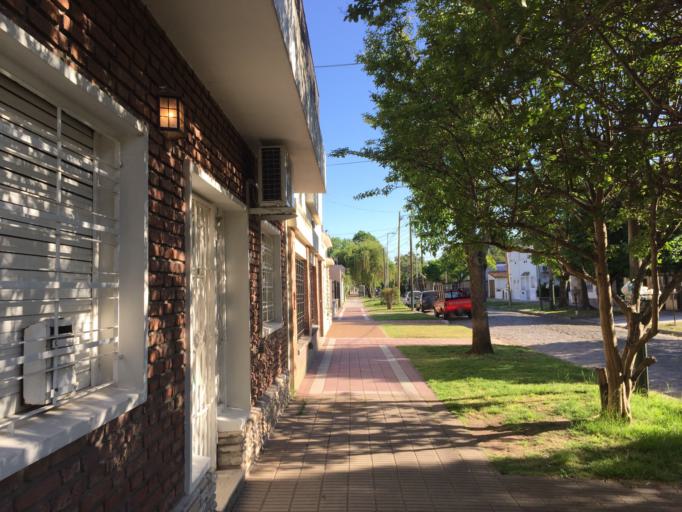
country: AR
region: Buenos Aires
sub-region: Partido de Lomas de Zamora
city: Lomas de Zamora
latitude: -34.7392
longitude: -58.3879
